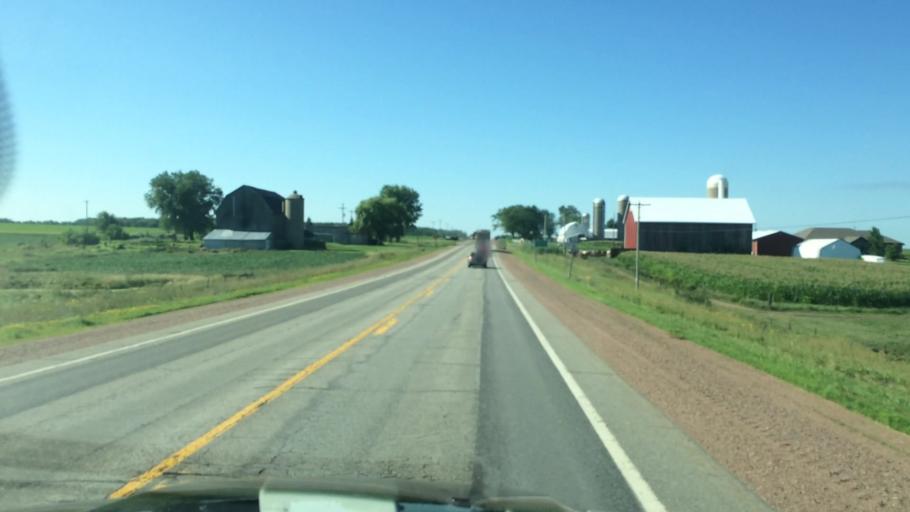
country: US
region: Wisconsin
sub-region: Marathon County
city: Stratford
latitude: 44.9046
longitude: -90.0787
